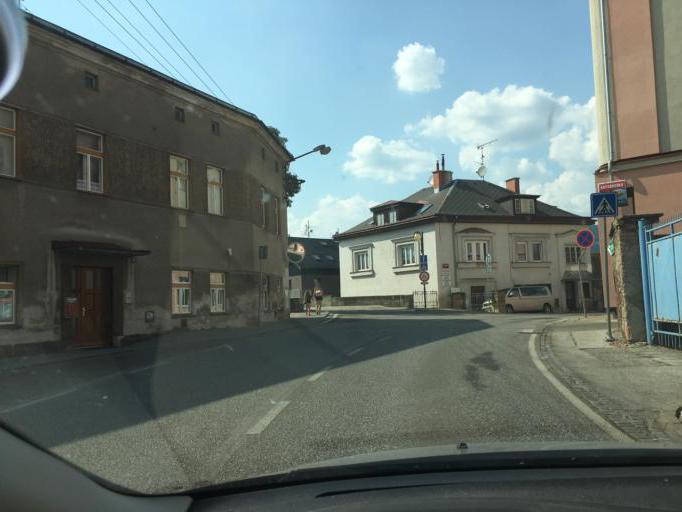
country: CZ
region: Kralovehradecky
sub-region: Okres Trutnov
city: Vrchlabi
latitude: 50.6226
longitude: 15.6153
